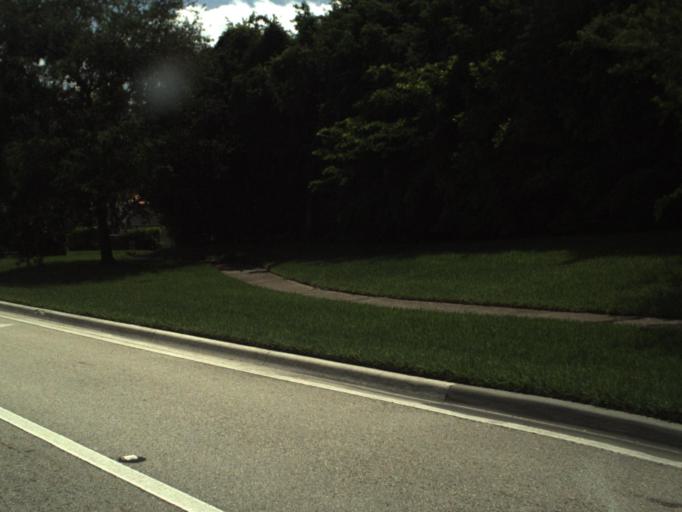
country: US
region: Florida
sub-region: Broward County
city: Tamarac
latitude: 26.2318
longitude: -80.2531
